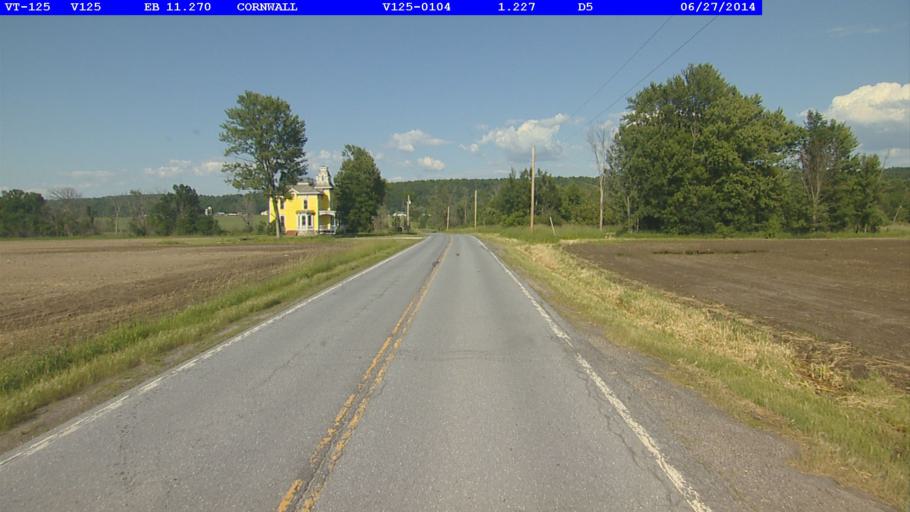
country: US
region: Vermont
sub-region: Addison County
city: Middlebury (village)
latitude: 43.9920
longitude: -73.2387
